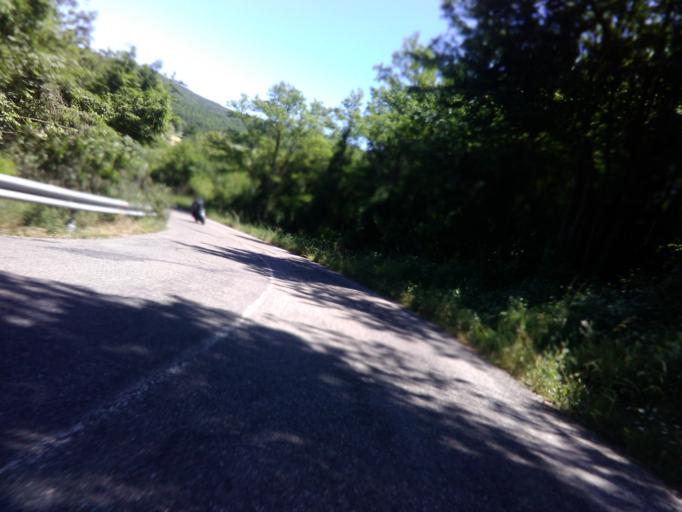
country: IT
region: Emilia-Romagna
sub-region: Provincia di Parma
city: Calestano
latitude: 44.5908
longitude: 10.1151
